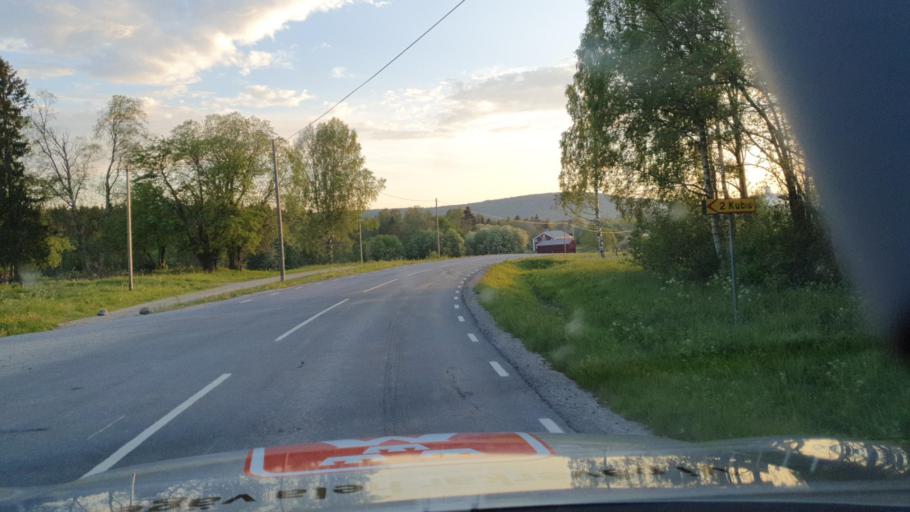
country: SE
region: Vaesternorrland
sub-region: OErnskoeldsviks Kommun
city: Bjasta
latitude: 63.2015
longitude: 18.5256
